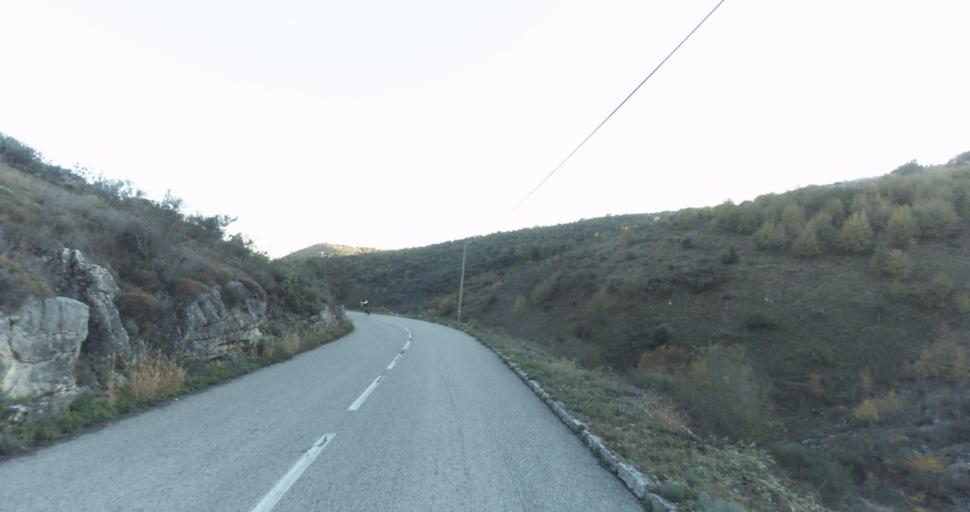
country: FR
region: Provence-Alpes-Cote d'Azur
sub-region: Departement des Alpes-Maritimes
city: Vence
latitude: 43.7525
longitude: 7.0947
